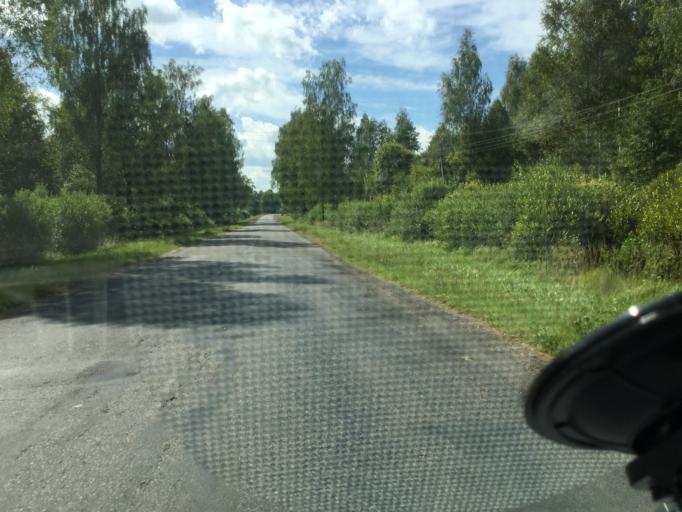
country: BY
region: Vitebsk
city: Chashniki
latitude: 55.2856
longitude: 29.3571
